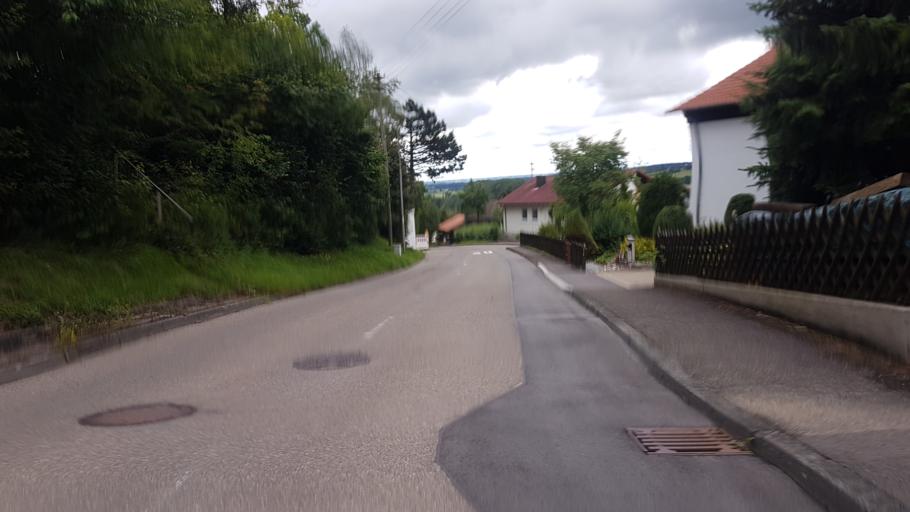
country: DE
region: Baden-Wuerttemberg
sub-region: Tuebingen Region
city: Ehingen
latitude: 48.2795
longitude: 9.7545
